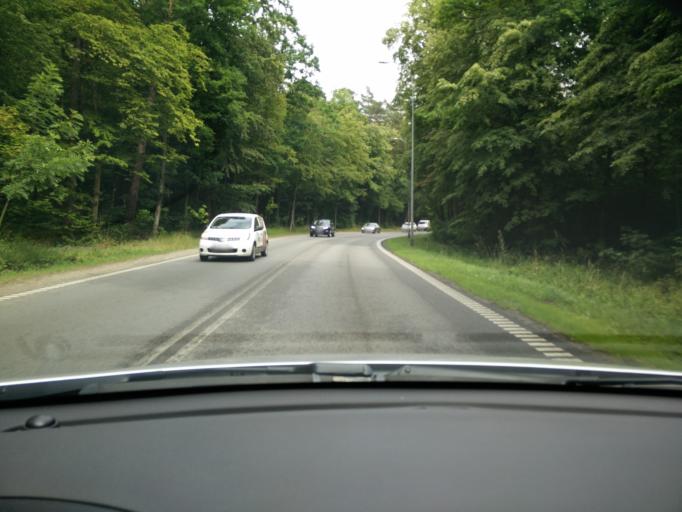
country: PL
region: Pomeranian Voivodeship
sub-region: Sopot
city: Sopot
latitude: 54.4229
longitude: 18.5307
